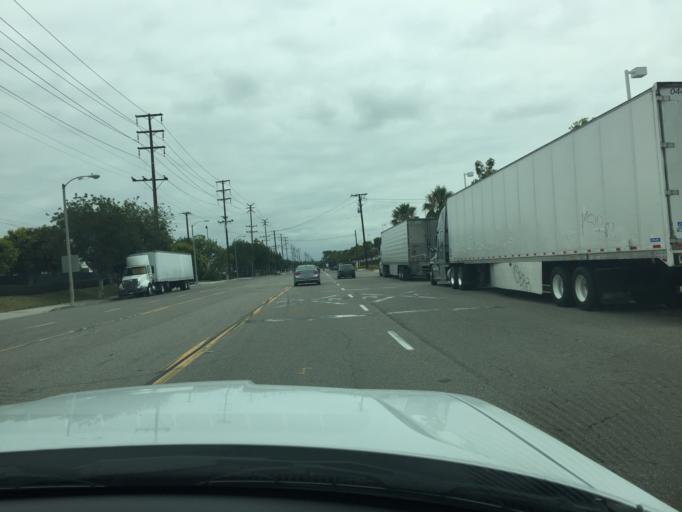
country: US
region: California
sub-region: Los Angeles County
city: Carson
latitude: 33.8317
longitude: -118.2363
